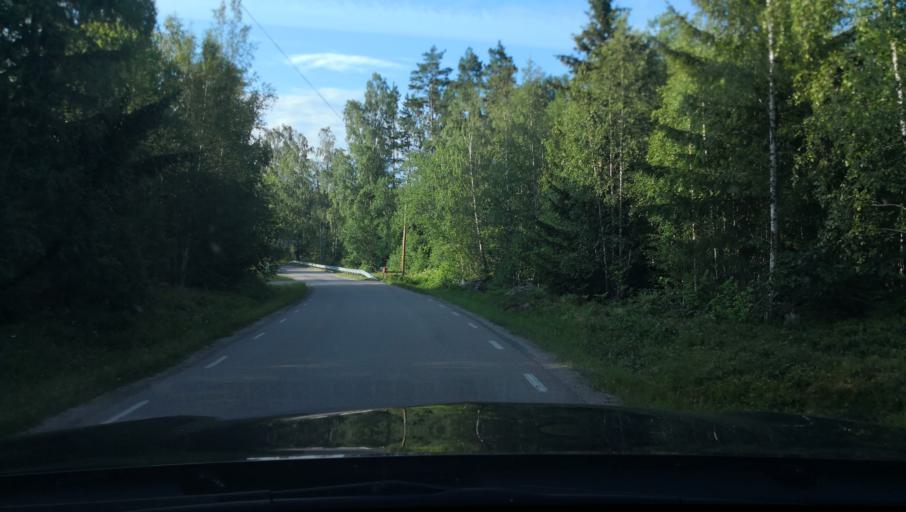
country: SE
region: Uppsala
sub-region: Osthammars Kommun
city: Osterbybruk
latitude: 60.0190
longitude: 17.9234
